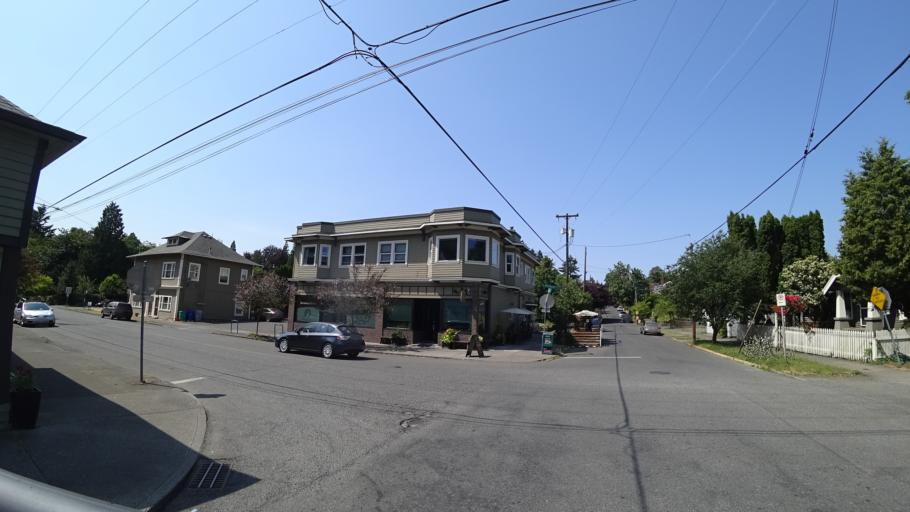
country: US
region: Oregon
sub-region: Multnomah County
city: Lents
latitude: 45.5168
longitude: -122.5923
